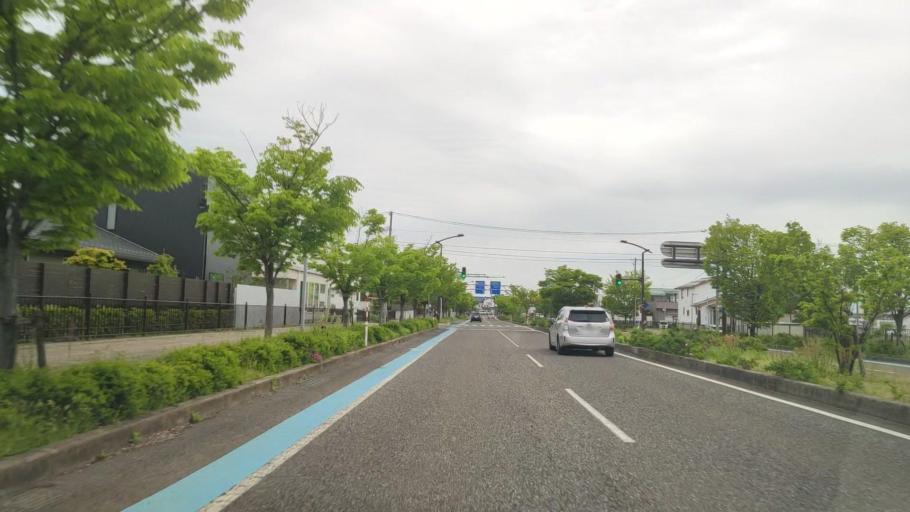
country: JP
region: Niigata
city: Kameda-honcho
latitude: 37.8845
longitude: 139.0704
